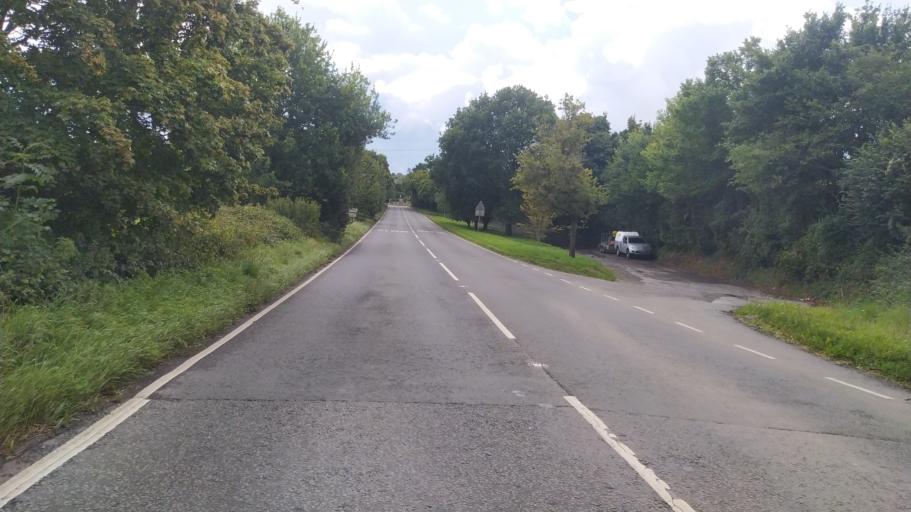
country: GB
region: England
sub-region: Dorset
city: Blandford Forum
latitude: 50.8814
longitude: -2.2070
